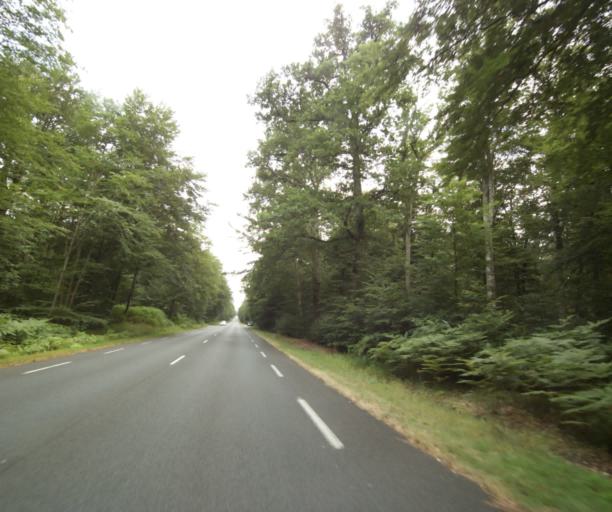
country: FR
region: Ile-de-France
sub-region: Departement de Seine-et-Marne
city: Bois-le-Roi
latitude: 48.4702
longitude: 2.6800
